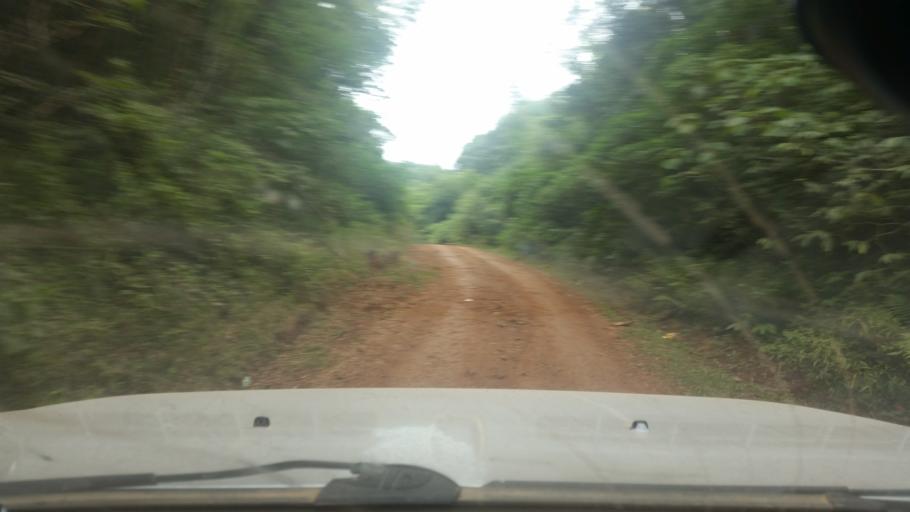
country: PY
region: Guaira
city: Independencia
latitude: -25.8071
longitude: -56.2730
